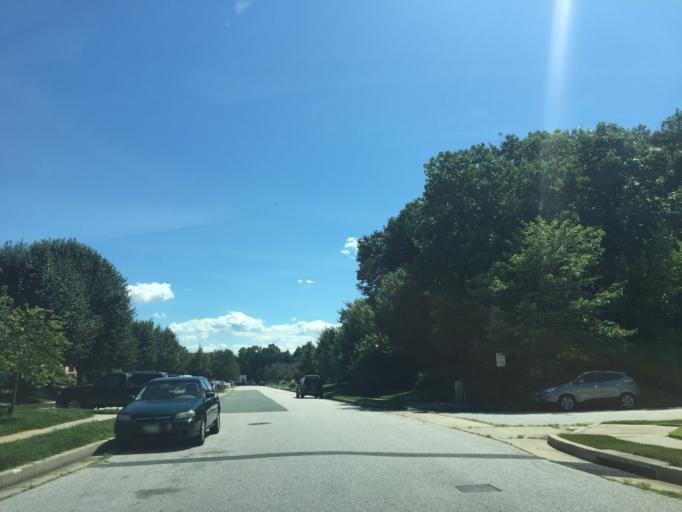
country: US
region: Maryland
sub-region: Baltimore County
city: Carney
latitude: 39.4022
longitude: -76.4967
